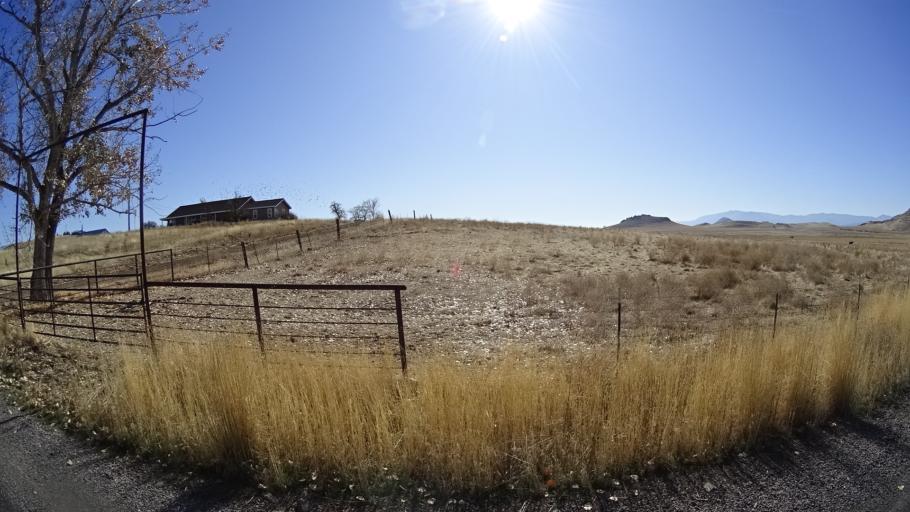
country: US
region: California
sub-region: Siskiyou County
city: Montague
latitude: 41.7559
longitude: -122.4735
